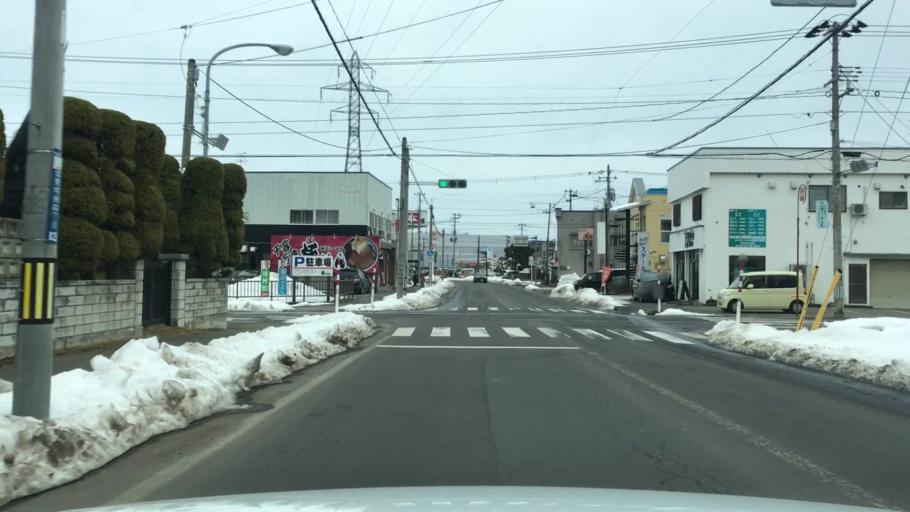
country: JP
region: Aomori
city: Hirosaki
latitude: 40.6000
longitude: 140.4975
